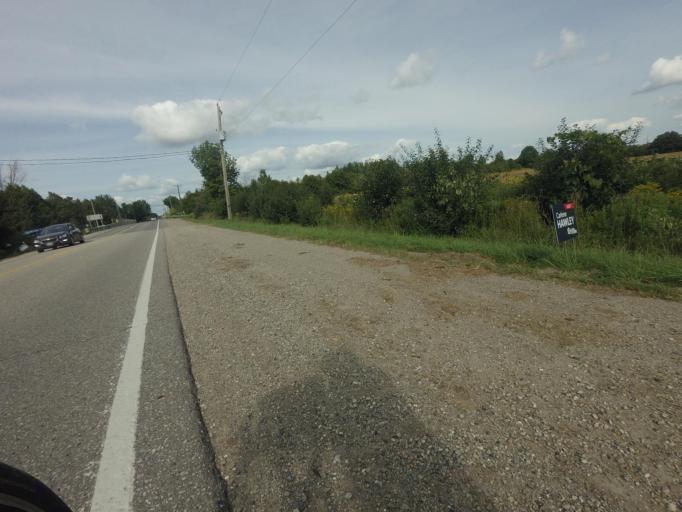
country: CA
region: Ontario
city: Waterloo
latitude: 43.5912
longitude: -80.4639
